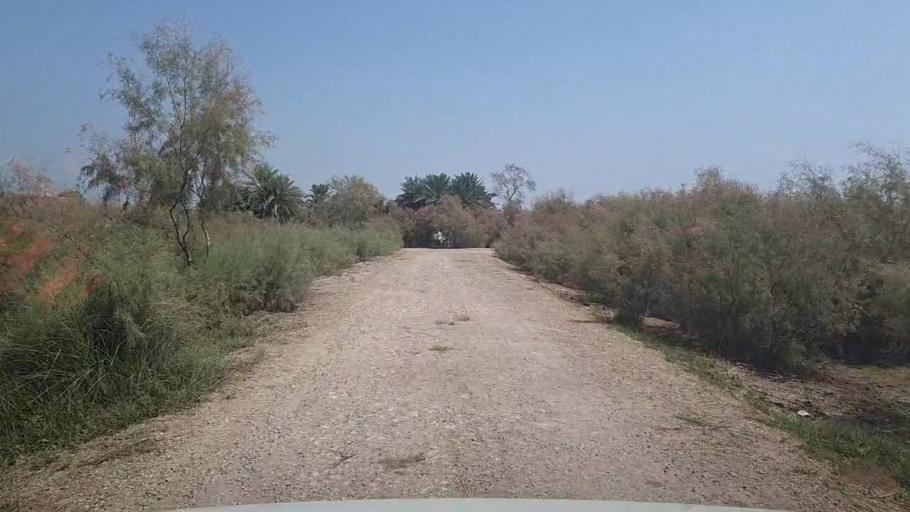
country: PK
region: Sindh
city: Kandhkot
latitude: 28.3062
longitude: 69.3579
